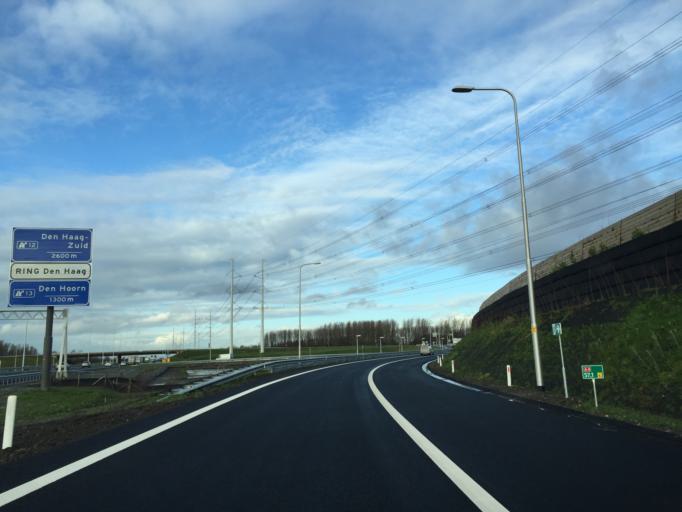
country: NL
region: South Holland
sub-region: Gemeente Delft
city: Delft
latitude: 51.9807
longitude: 4.3322
